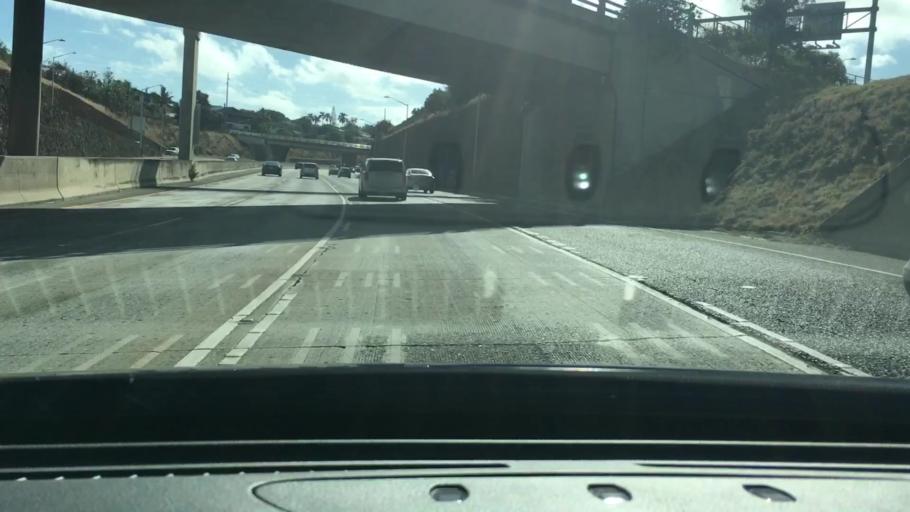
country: US
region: Hawaii
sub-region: Honolulu County
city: Honolulu
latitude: 21.2792
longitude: -157.7919
